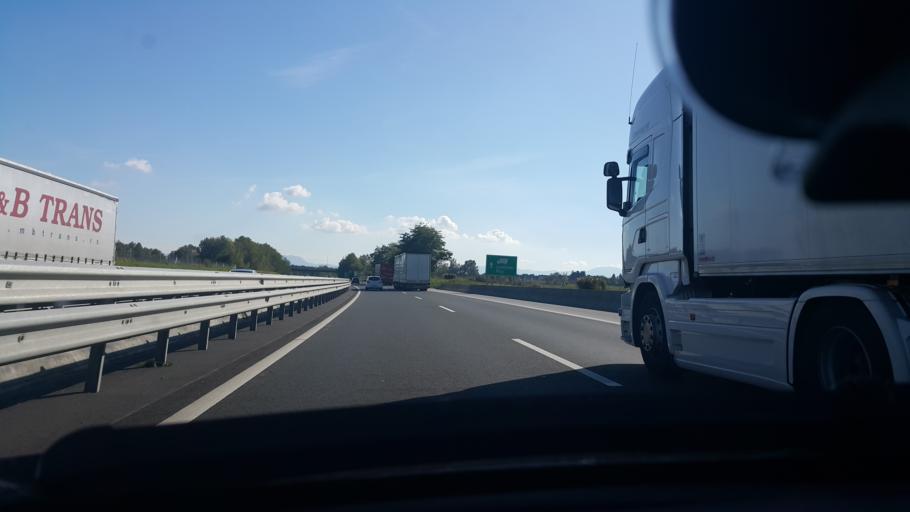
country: SI
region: Hoce-Slivnica
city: Rogoza
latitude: 46.5052
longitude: 15.6689
